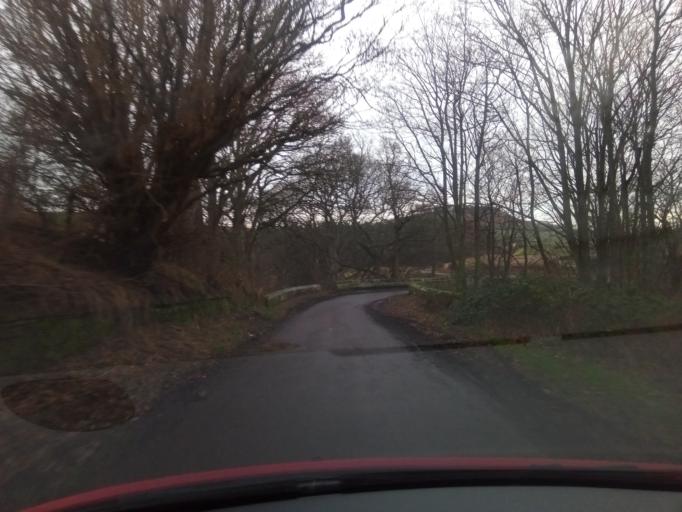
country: GB
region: England
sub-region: Northumberland
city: Wooler
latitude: 55.4957
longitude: -1.9121
